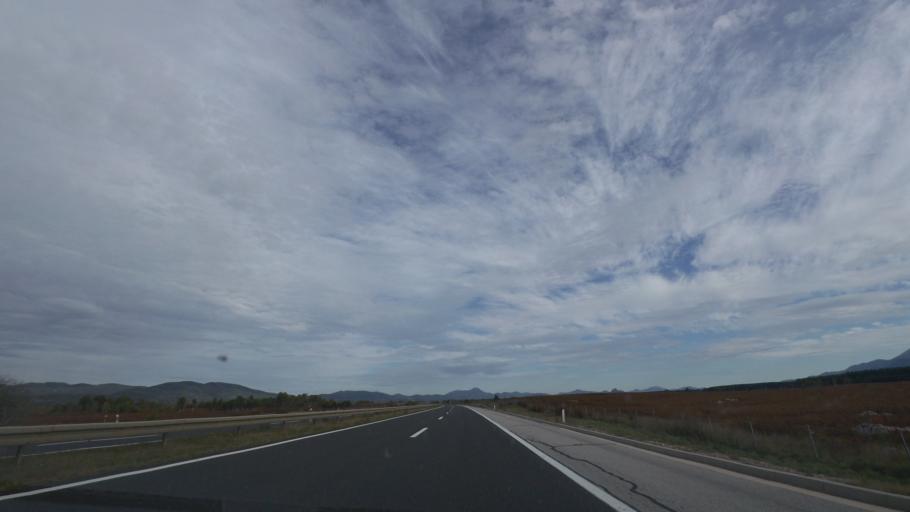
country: HR
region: Licko-Senjska
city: Gospic
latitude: 44.5195
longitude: 15.4711
